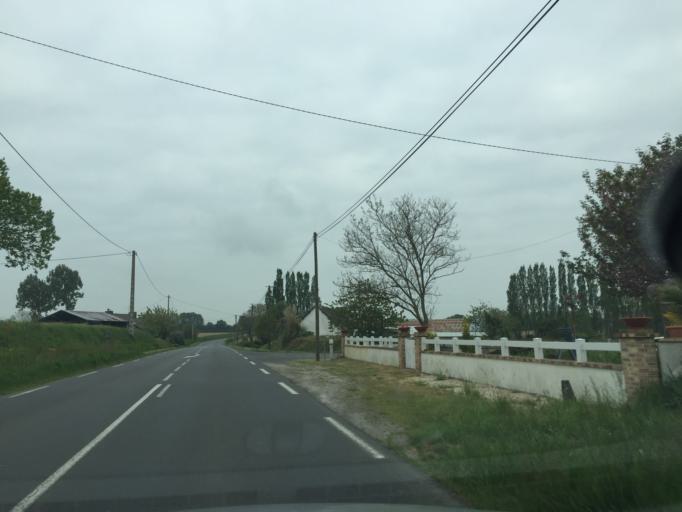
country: FR
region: Brittany
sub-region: Departement des Cotes-d'Armor
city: Matignon
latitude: 48.5850
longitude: -2.3229
